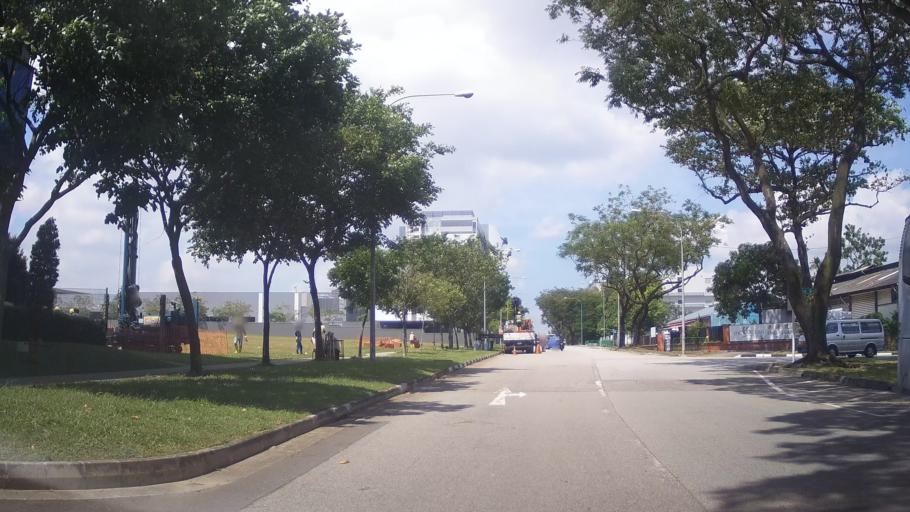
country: SG
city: Singapore
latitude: 1.3264
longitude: 103.7139
